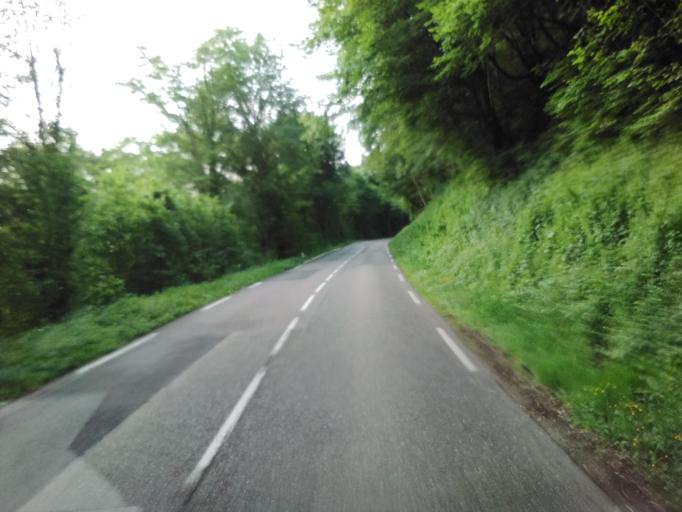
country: FR
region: Franche-Comte
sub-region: Departement du Jura
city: Arbois
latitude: 46.8963
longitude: 5.7936
